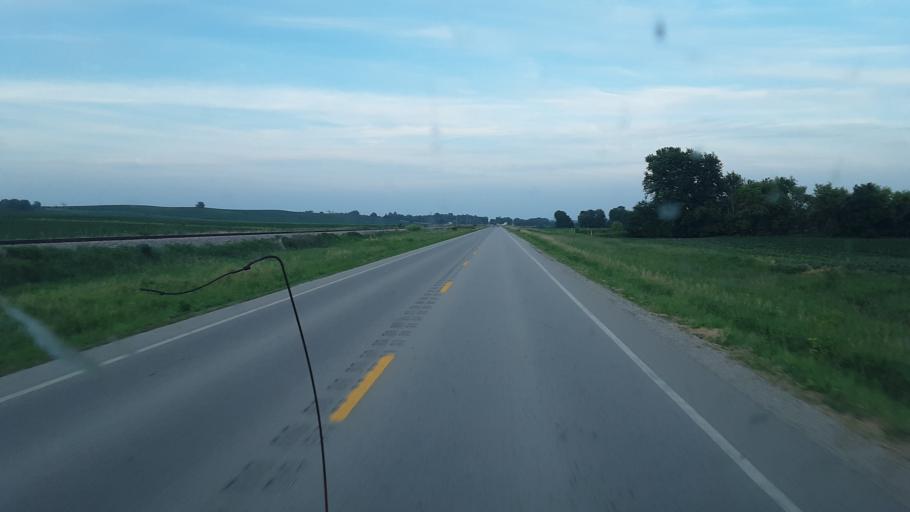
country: US
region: Iowa
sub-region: Iowa County
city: Marengo
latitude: 41.7487
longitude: -92.2138
